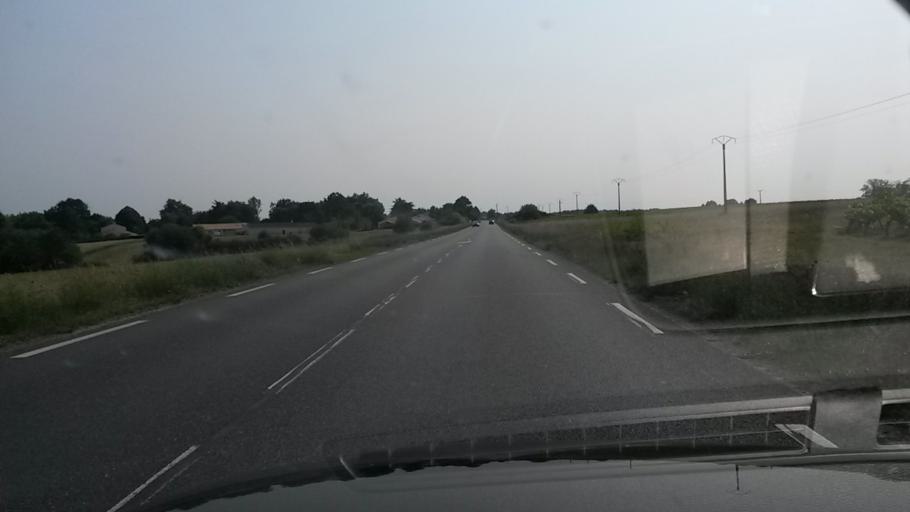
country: FR
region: Pays de la Loire
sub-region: Departement de la Loire-Atlantique
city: Mouzillon
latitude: 47.1497
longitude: -1.2798
